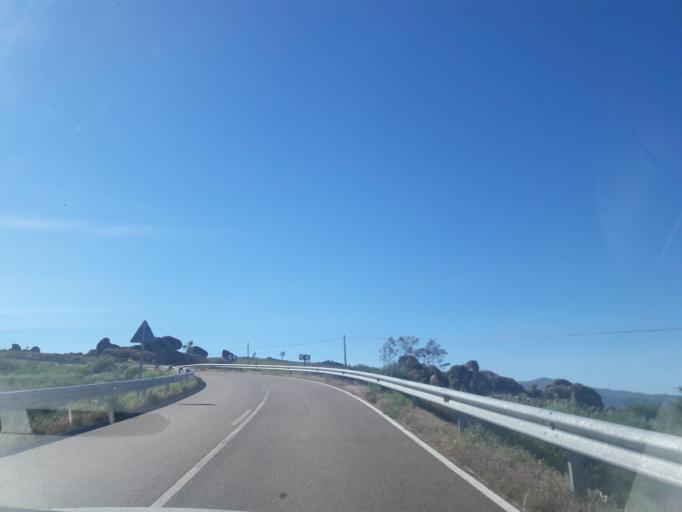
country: ES
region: Castille and Leon
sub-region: Provincia de Salamanca
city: Lagunilla
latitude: 40.3249
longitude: -5.9341
